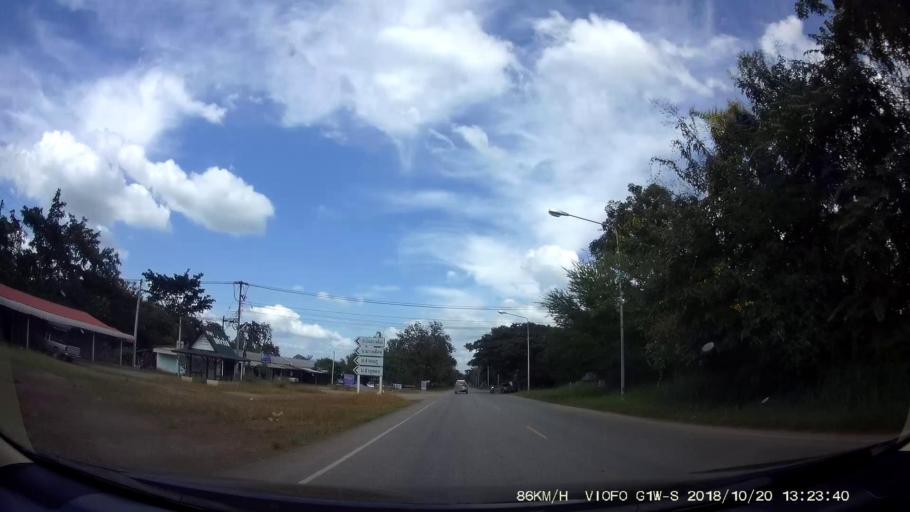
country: TH
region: Chaiyaphum
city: Khon San
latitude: 16.5861
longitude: 101.9227
